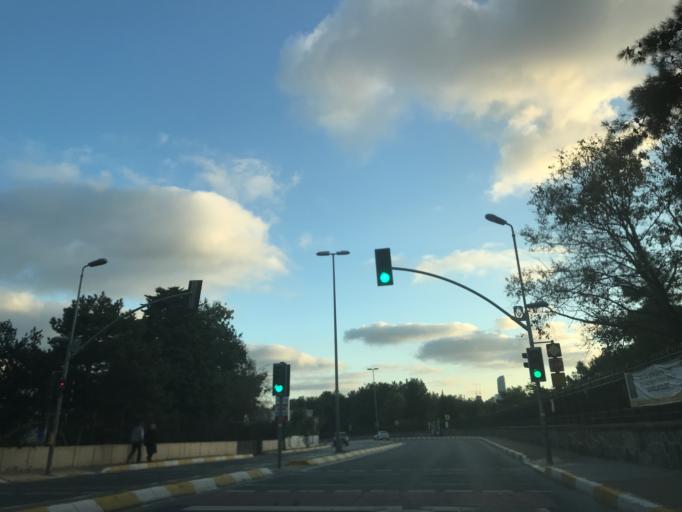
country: TR
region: Istanbul
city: Sisli
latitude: 41.1348
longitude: 29.0397
